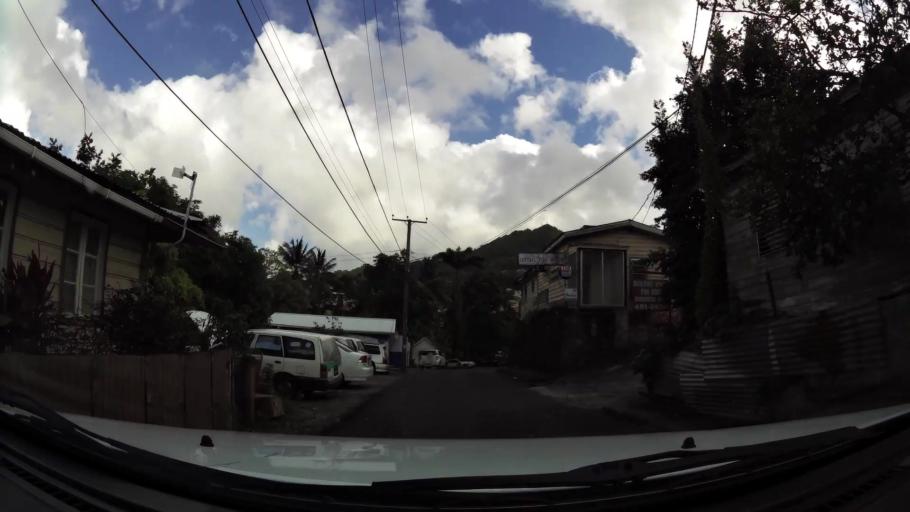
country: LC
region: Castries Quarter
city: Bisee
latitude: 14.0031
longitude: -60.9840
